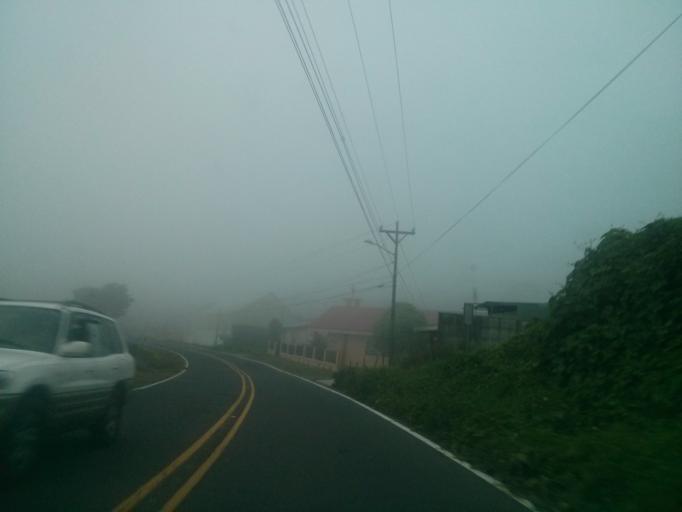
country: CR
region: Cartago
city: Cot
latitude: 9.8984
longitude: -83.8341
